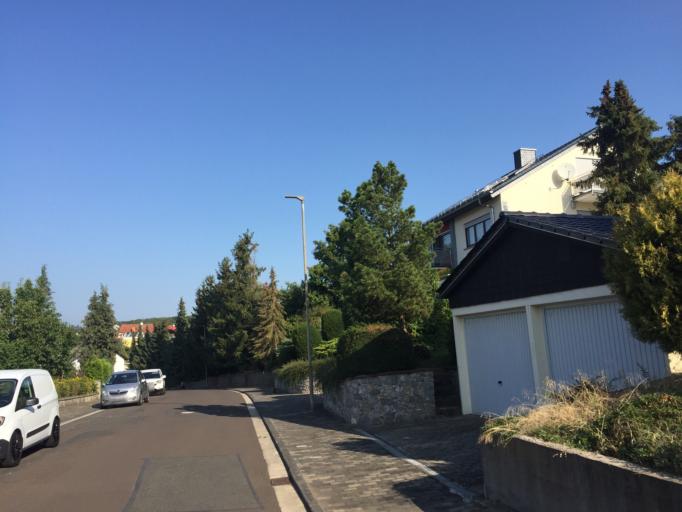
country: DE
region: Hesse
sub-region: Regierungsbezirk Giessen
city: Hoernsheim
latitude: 50.4629
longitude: 8.5891
